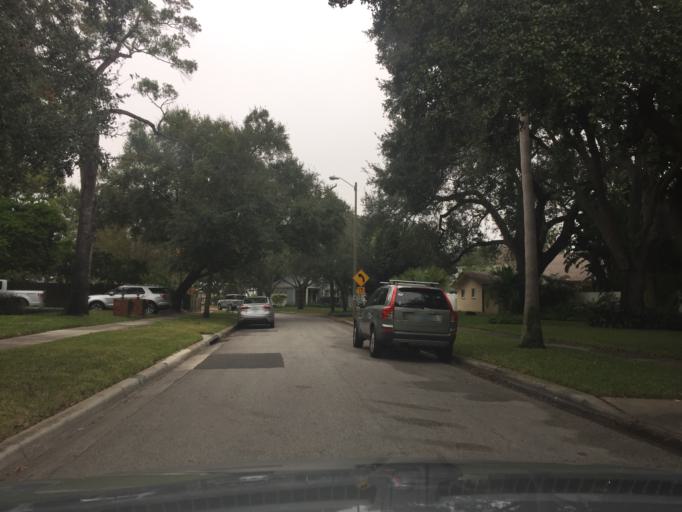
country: US
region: Florida
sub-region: Hillsborough County
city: Tampa
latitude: 27.9362
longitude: -82.4856
